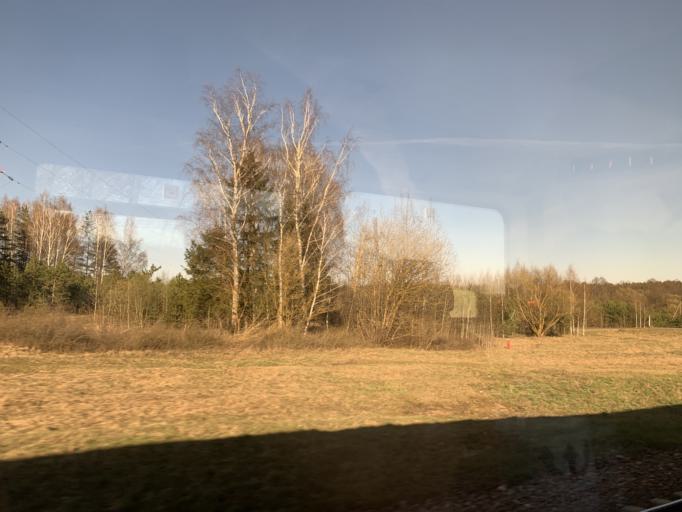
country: BY
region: Grodnenskaya
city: Smarhon'
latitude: 54.4332
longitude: 26.5199
